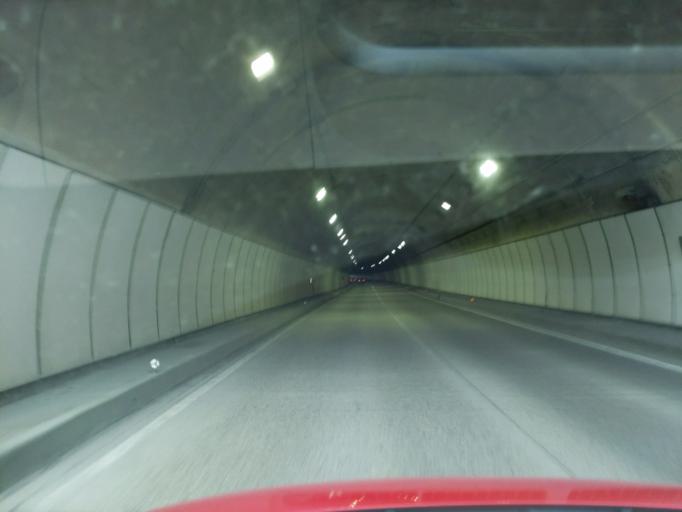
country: JP
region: Gifu
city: Tajimi
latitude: 35.3278
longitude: 137.0624
